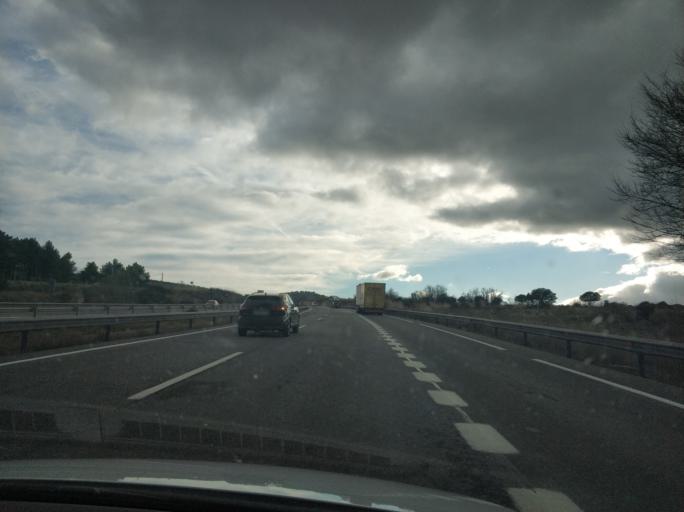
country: ES
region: Madrid
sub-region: Provincia de Madrid
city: Buitrago del Lozoya
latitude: 40.9751
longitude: -3.6395
